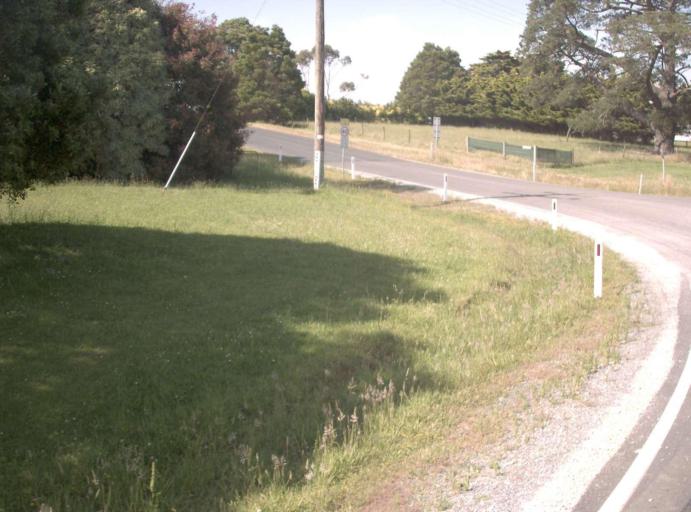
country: AU
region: Victoria
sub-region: Baw Baw
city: Warragul
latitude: -38.3433
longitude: 145.7694
